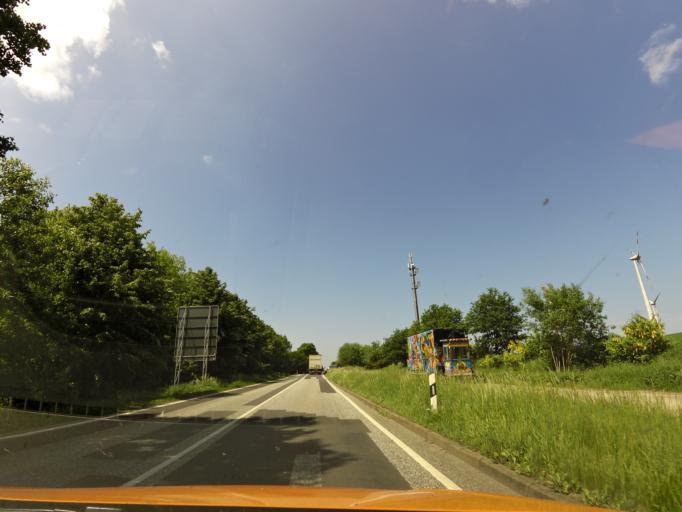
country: DE
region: Mecklenburg-Vorpommern
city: Selmsdorf
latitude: 53.8668
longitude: 10.9017
